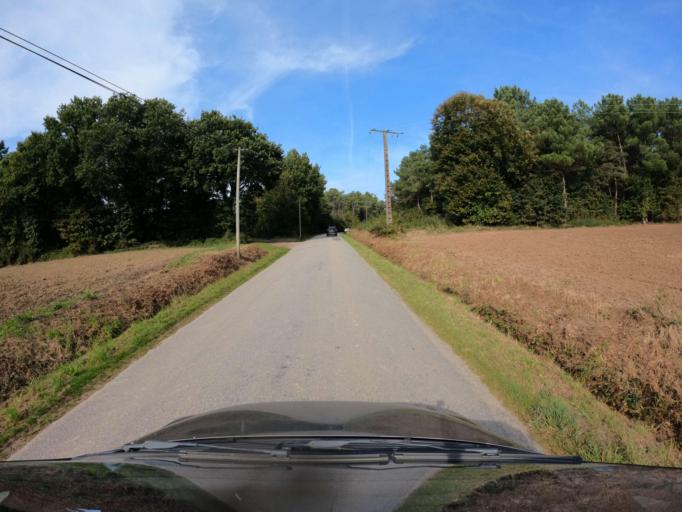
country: FR
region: Brittany
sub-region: Departement du Morbihan
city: Ploermel
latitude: 47.8770
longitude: -2.4039
